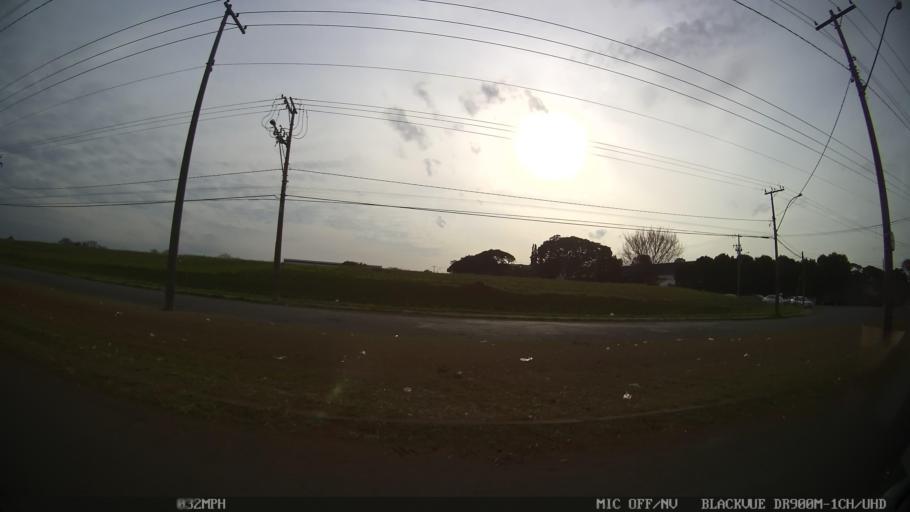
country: BR
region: Sao Paulo
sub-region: Piracicaba
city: Piracicaba
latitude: -22.7323
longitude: -47.5878
